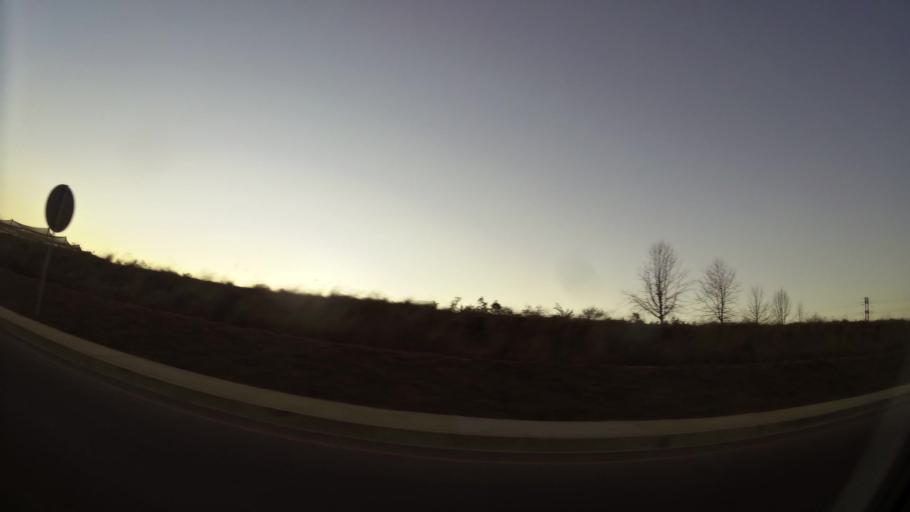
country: ZA
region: Gauteng
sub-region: City of Johannesburg Metropolitan Municipality
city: Diepsloot
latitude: -25.9730
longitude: 28.0212
